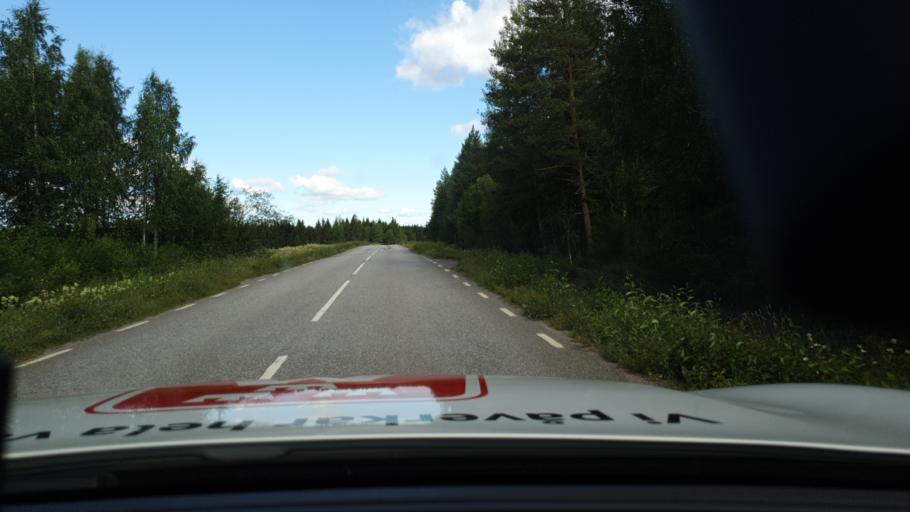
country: SE
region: Norrbotten
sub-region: Lulea Kommun
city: Ranea
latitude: 65.8893
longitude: 22.1919
